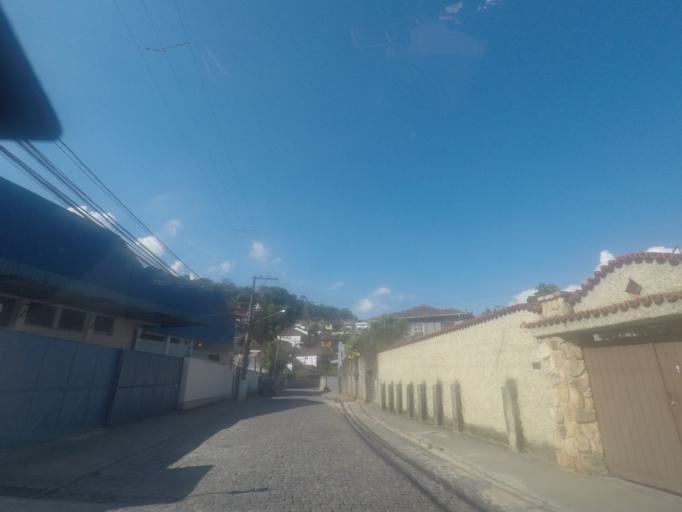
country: BR
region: Rio de Janeiro
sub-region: Petropolis
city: Petropolis
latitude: -22.5375
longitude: -43.1997
